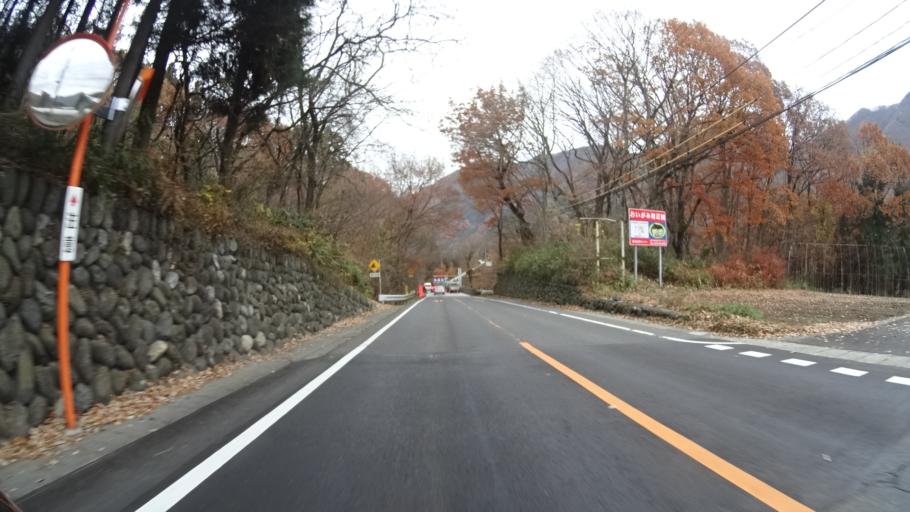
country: JP
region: Gunma
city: Numata
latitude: 36.6788
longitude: 139.2049
